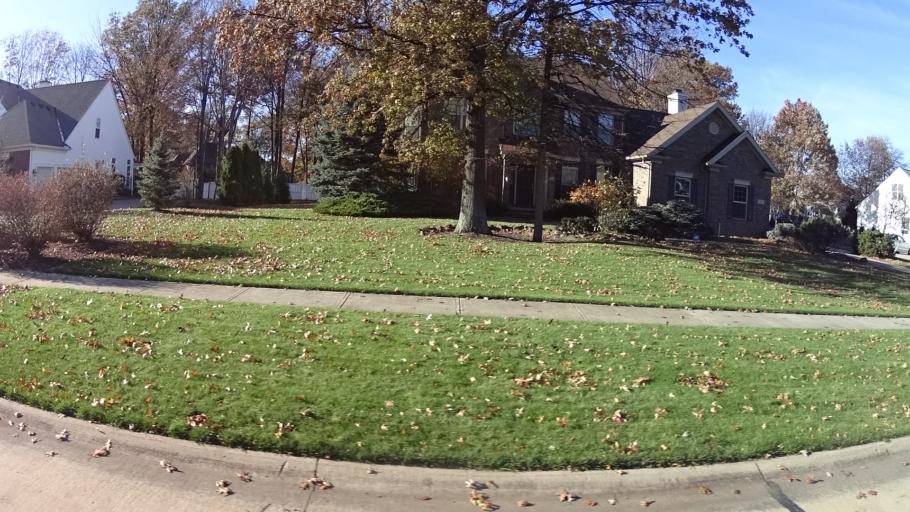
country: US
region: Ohio
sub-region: Lorain County
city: Avon Lake
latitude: 41.5008
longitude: -81.9943
